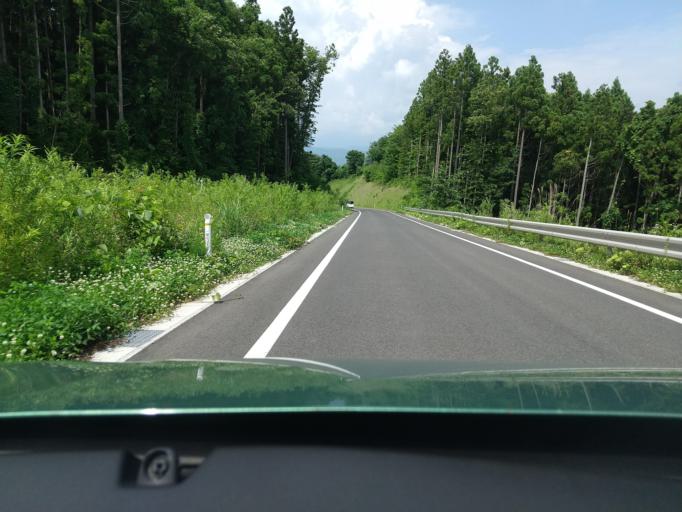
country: JP
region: Iwate
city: Ichinoseki
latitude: 38.9901
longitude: 141.2178
